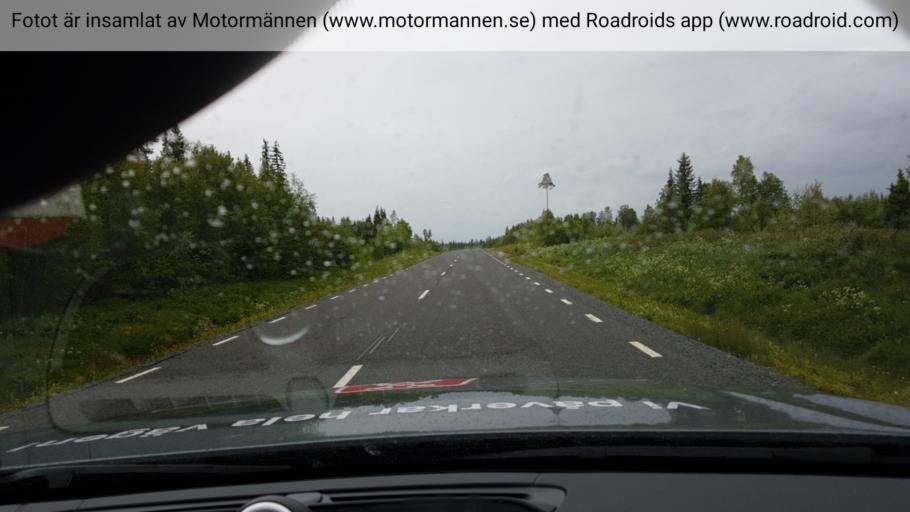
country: SE
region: Jaemtland
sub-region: Stroemsunds Kommun
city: Stroemsund
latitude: 63.6420
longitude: 15.1825
